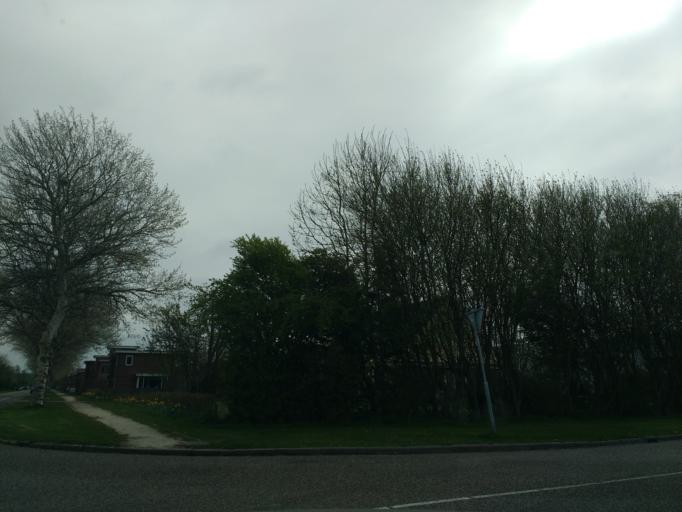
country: NL
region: North Holland
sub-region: Gemeente Schagen
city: Harenkarspel
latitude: 52.7160
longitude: 4.7281
